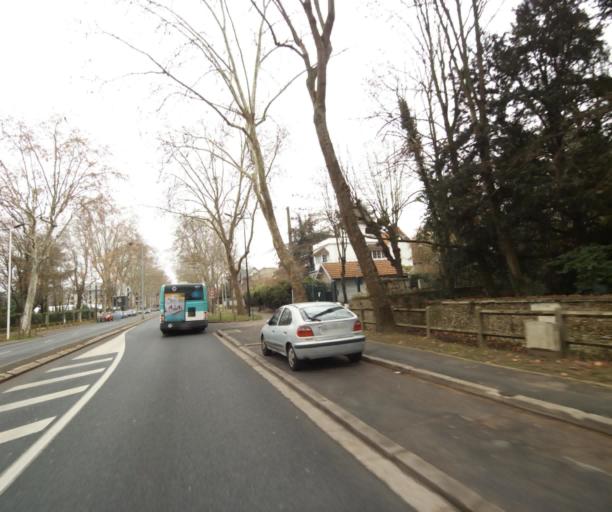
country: FR
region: Ile-de-France
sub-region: Departement des Yvelines
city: Chatou
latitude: 48.8709
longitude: 2.1599
